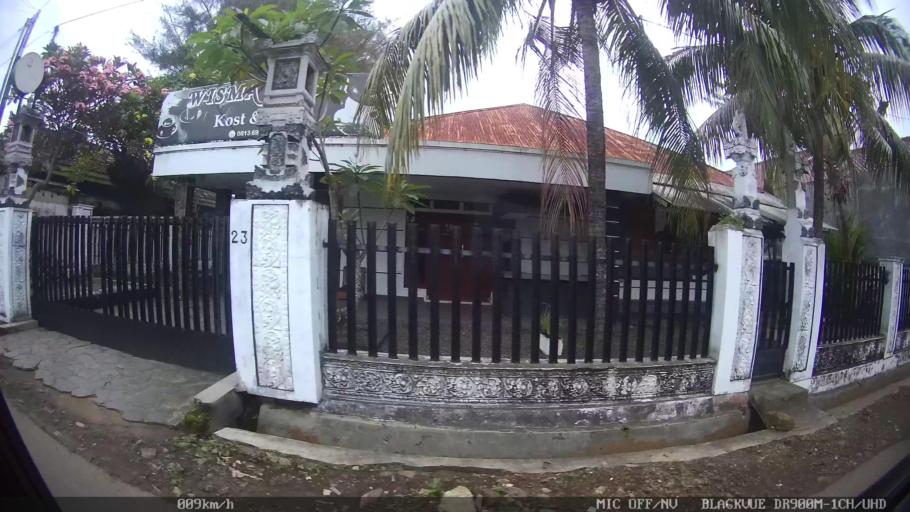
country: ID
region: Lampung
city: Kedaton
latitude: -5.3829
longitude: 105.2503
